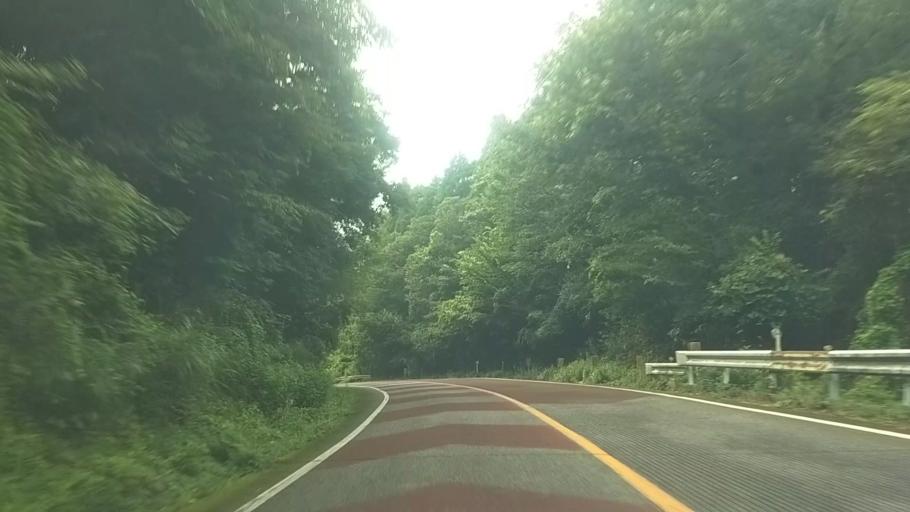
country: JP
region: Chiba
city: Kawaguchi
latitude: 35.2321
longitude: 140.0272
